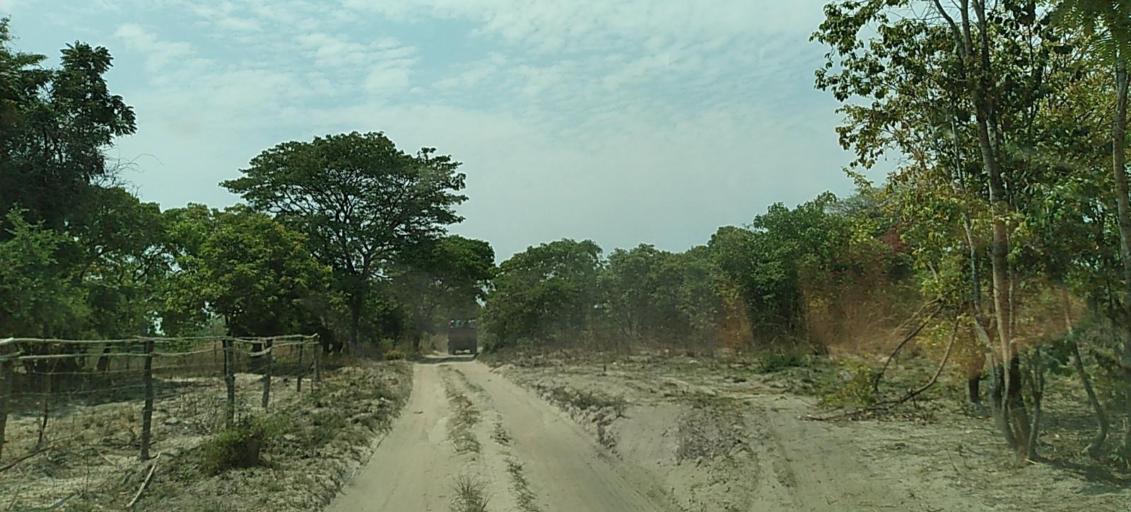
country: ZM
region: Copperbelt
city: Kalulushi
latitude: -12.9311
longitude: 28.1100
